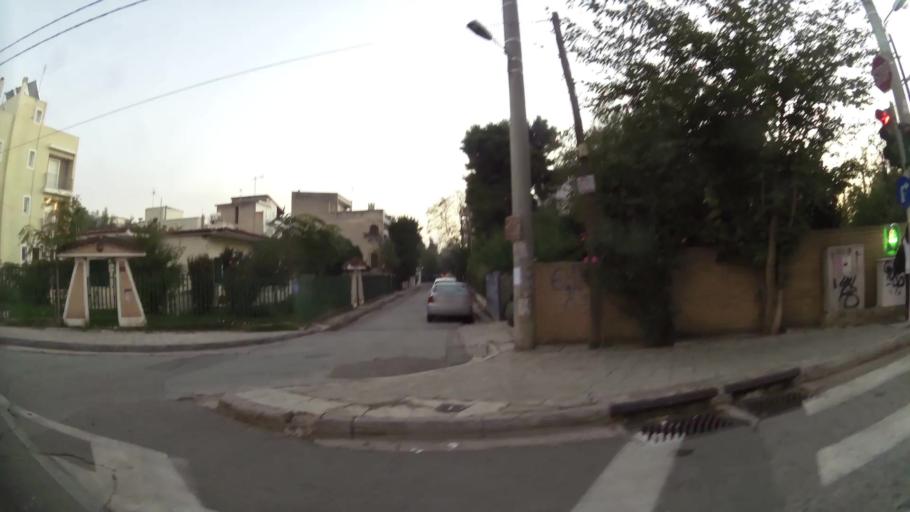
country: GR
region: Attica
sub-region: Nomarchia Athinas
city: Khalandrion
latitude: 38.0195
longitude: 23.8105
